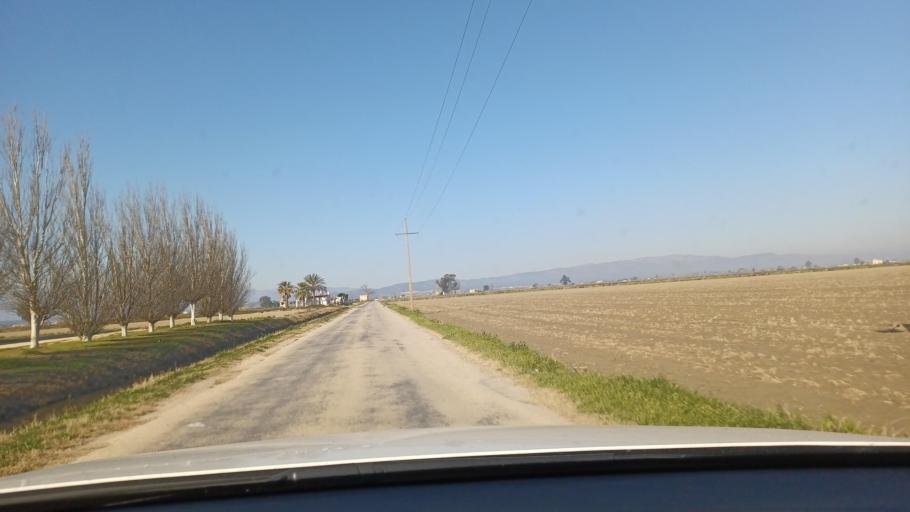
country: ES
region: Catalonia
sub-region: Provincia de Tarragona
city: Deltebre
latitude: 40.6820
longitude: 0.6574
